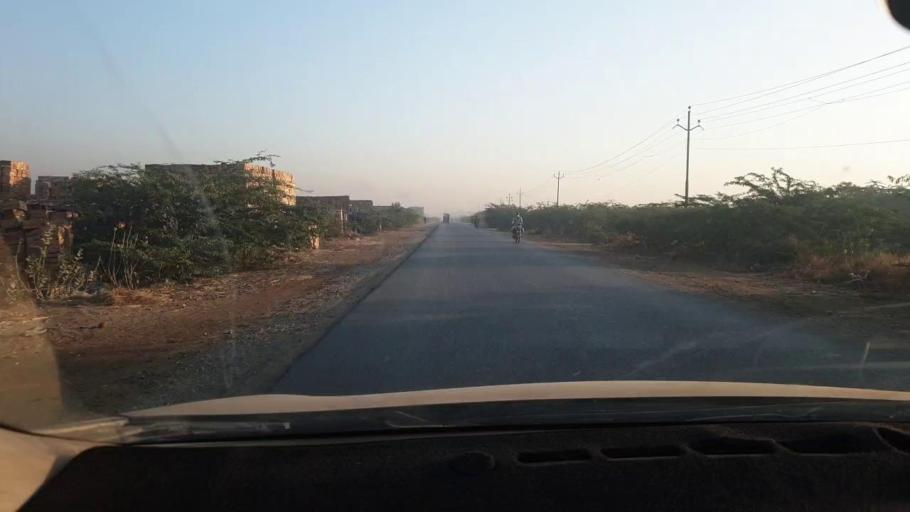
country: PK
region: Sindh
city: Malir Cantonment
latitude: 24.9987
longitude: 67.1453
